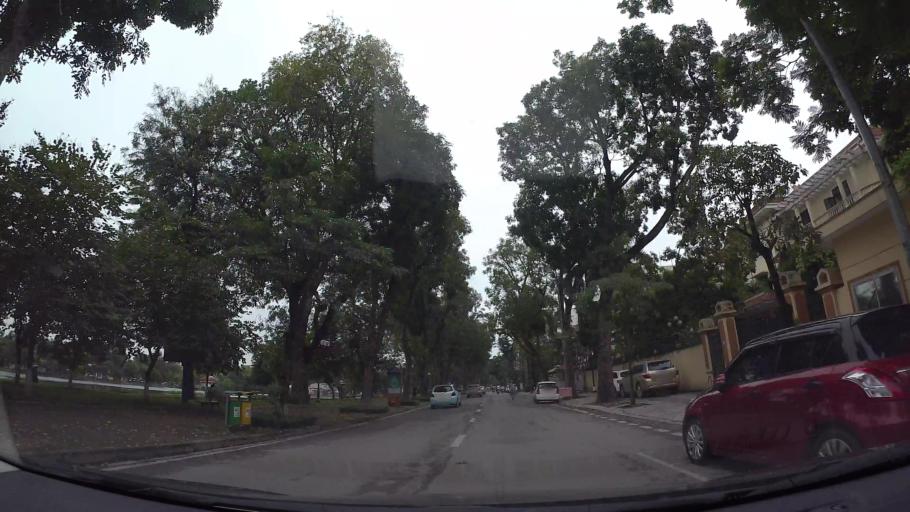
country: VN
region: Ha Noi
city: Hai BaTrung
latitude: 21.0192
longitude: 105.8472
